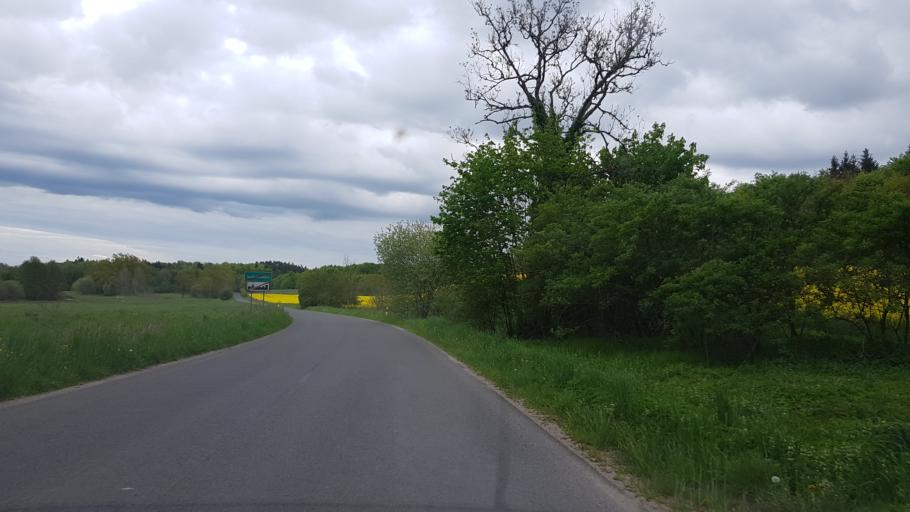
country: PL
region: West Pomeranian Voivodeship
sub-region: Powiat slawienski
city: Slawno
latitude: 54.2709
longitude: 16.5513
